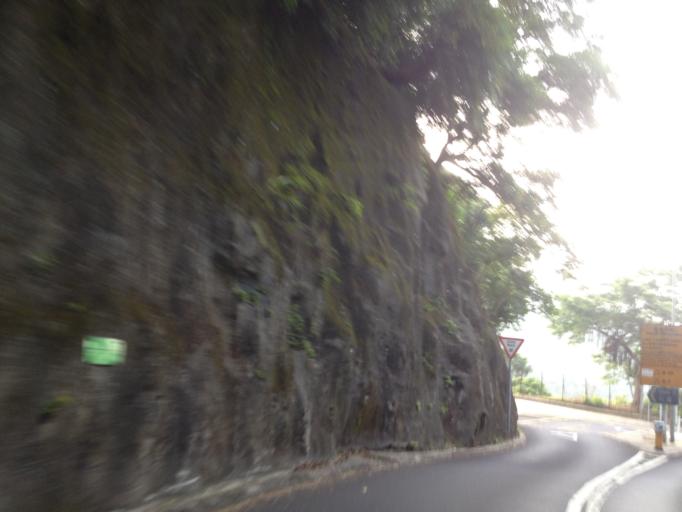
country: HK
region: Wanchai
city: Wan Chai
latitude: 22.2577
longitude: 114.2281
